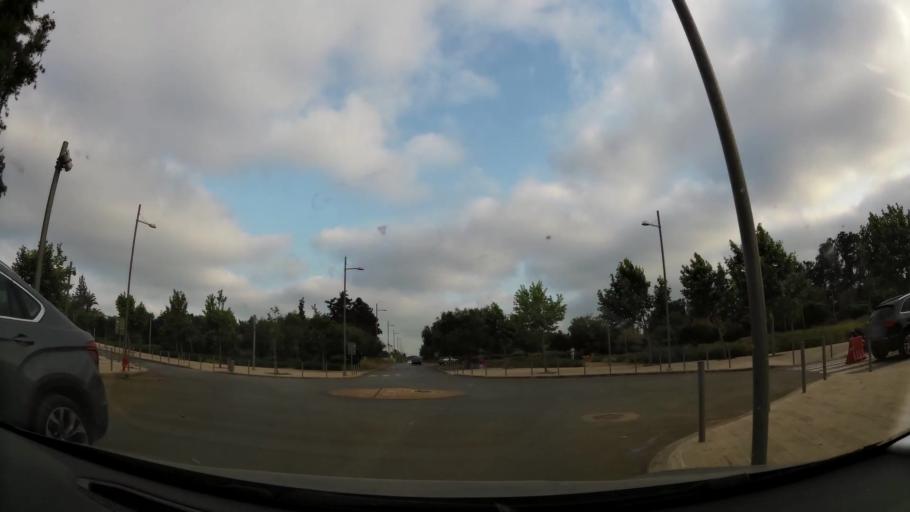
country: MA
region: Rabat-Sale-Zemmour-Zaer
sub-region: Rabat
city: Rabat
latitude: 33.9487
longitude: -6.8326
